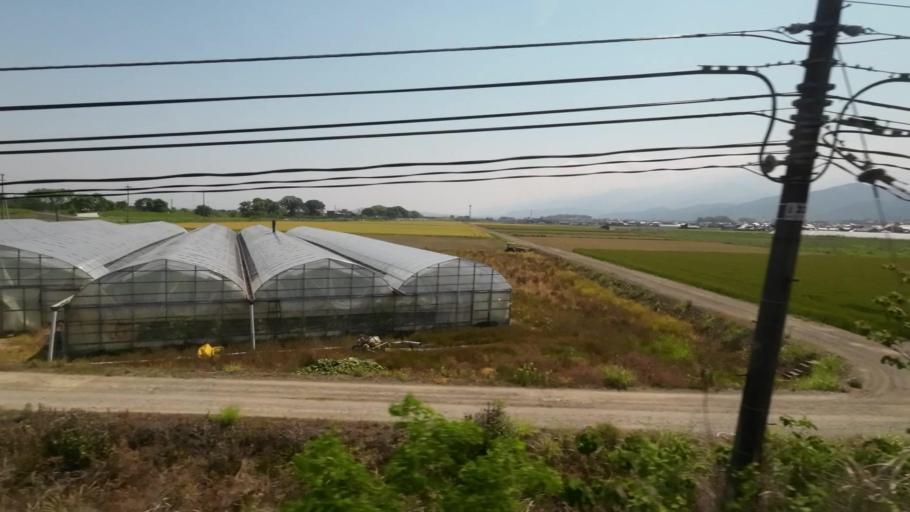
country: JP
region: Ehime
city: Saijo
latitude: 33.9030
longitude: 133.0995
